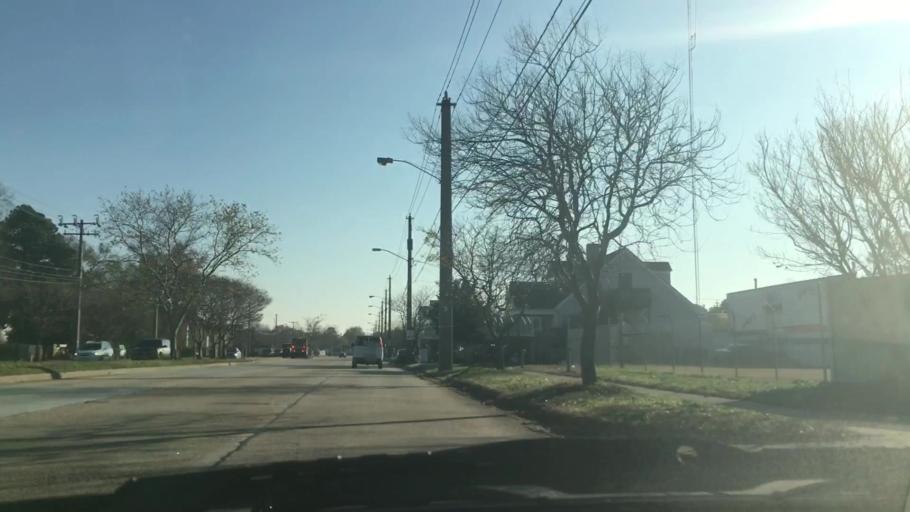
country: US
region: Virginia
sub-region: City of Norfolk
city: Norfolk
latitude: 36.8950
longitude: -76.2385
